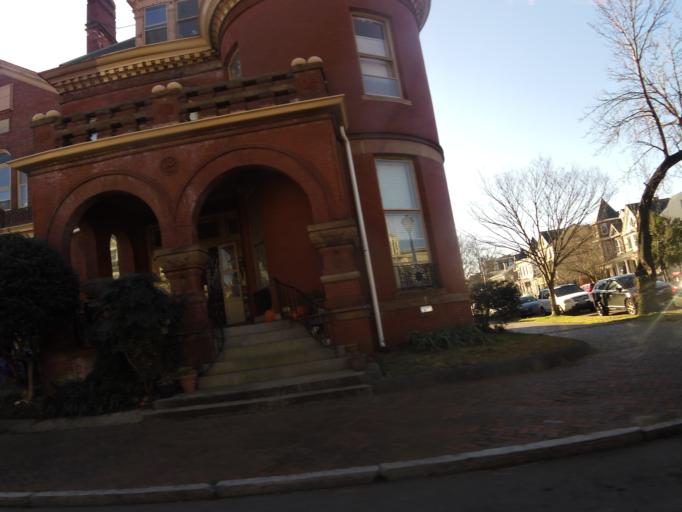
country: US
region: Virginia
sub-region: City of Portsmouth
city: Portsmouth
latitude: 36.8383
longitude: -76.3008
